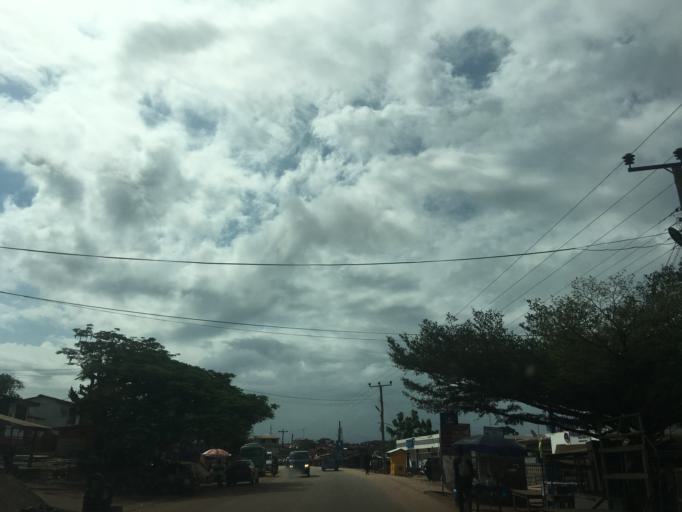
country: GH
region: Western
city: Wassa-Akropong
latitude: 5.8056
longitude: -2.4326
